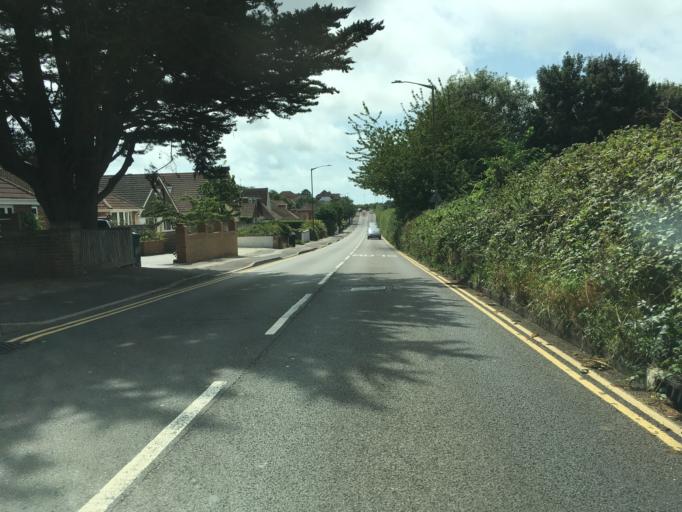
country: GB
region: England
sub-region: Brighton and Hove
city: Rottingdean
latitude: 50.8308
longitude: -0.0732
